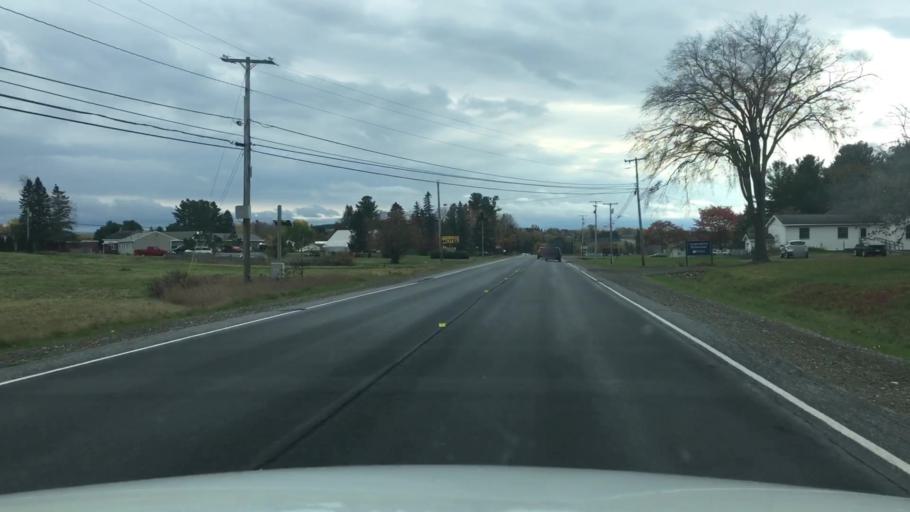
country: US
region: Maine
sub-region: Aroostook County
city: Presque Isle
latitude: 46.6560
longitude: -68.0059
